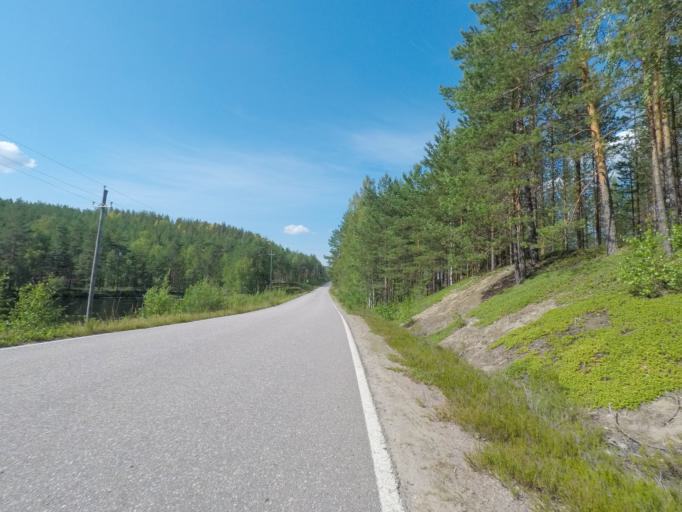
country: FI
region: Southern Savonia
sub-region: Mikkeli
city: Puumala
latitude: 61.4619
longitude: 28.1746
